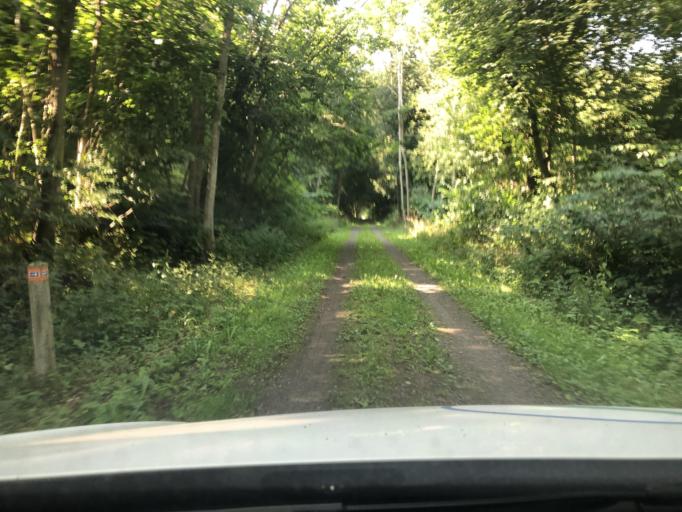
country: SE
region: Skane
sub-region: Kristianstads Kommun
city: Degeberga
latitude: 55.8048
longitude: 14.1374
